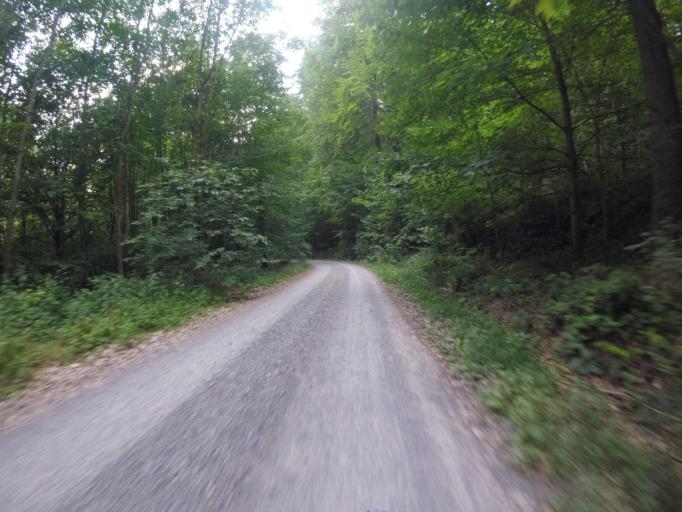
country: DE
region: Baden-Wuerttemberg
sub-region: Regierungsbezirk Stuttgart
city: Sulzbach an der Murr
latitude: 48.9679
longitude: 9.4964
